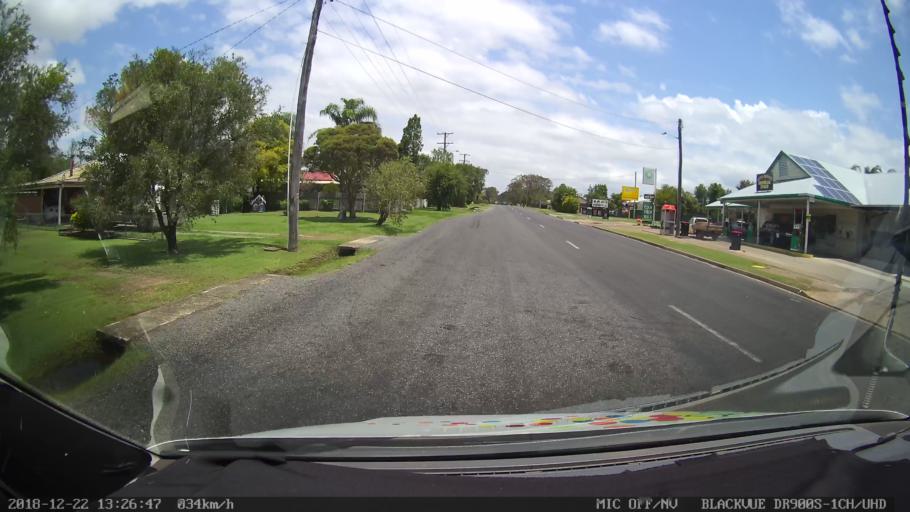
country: AU
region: New South Wales
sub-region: Clarence Valley
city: Coutts Crossing
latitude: -29.8278
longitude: 152.8918
